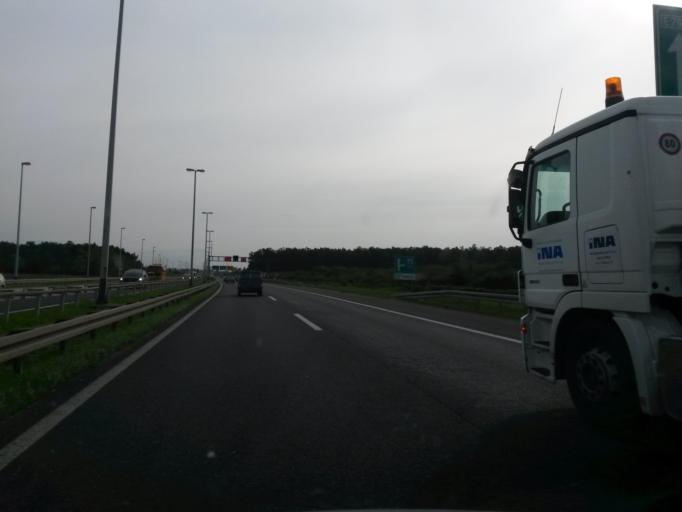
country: HR
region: Grad Zagreb
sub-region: Sesvete
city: Sesvete
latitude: 45.8083
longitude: 16.1336
